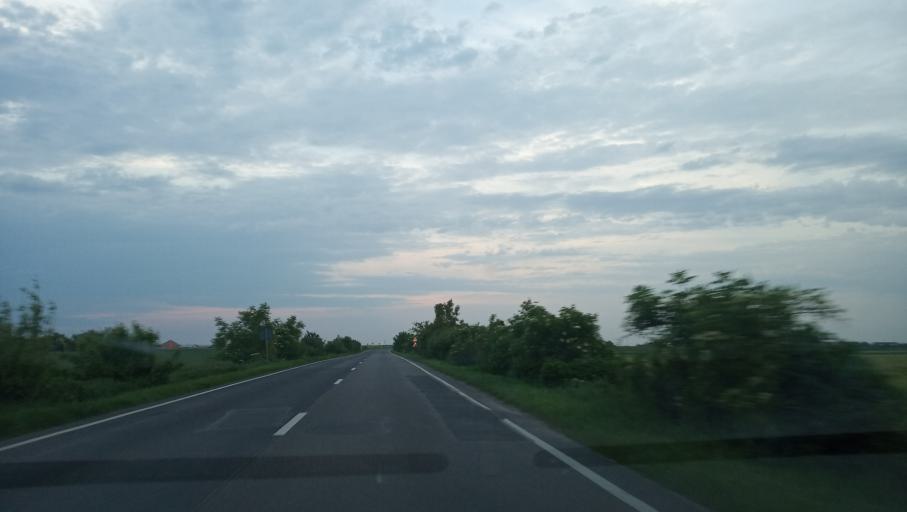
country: RO
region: Timis
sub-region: Comuna Voiteg
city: Voiteg
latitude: 45.4786
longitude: 21.2333
